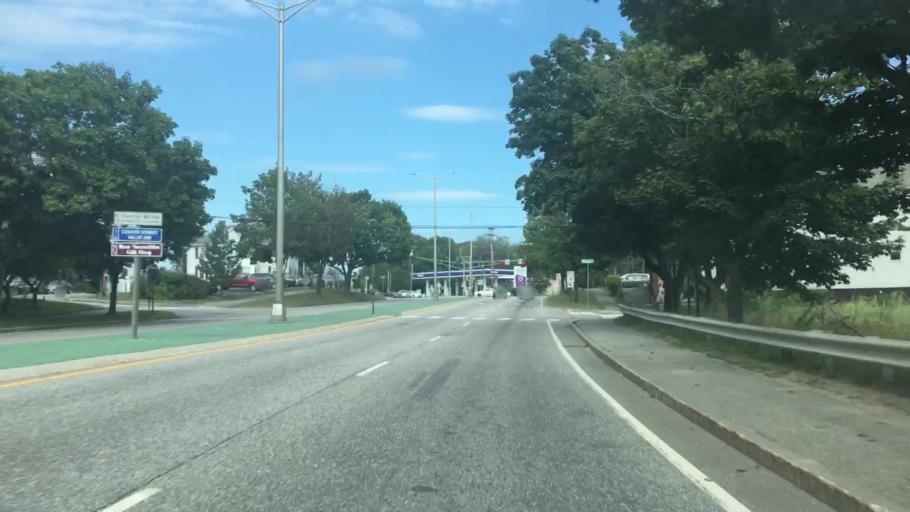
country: US
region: Maine
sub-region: Androscoggin County
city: Auburn
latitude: 44.1016
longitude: -70.2281
